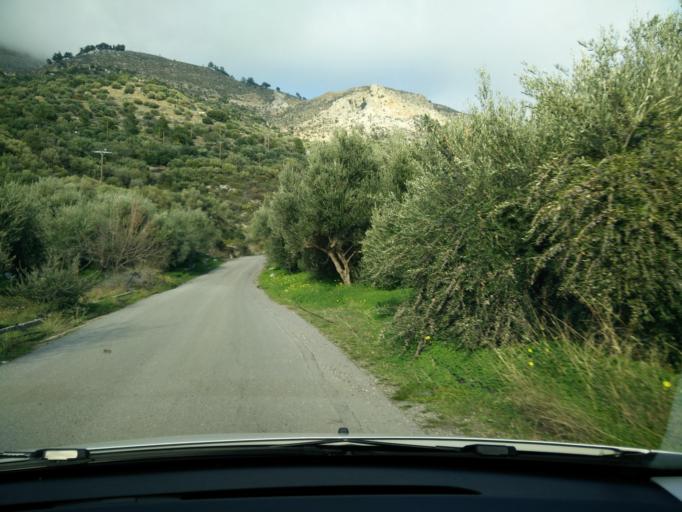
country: GR
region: Crete
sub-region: Nomos Lasithiou
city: Gra Liyia
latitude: 35.0258
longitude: 25.5468
